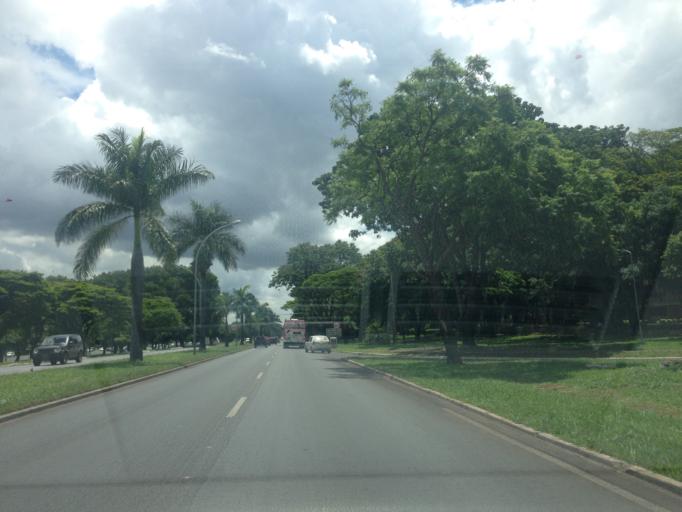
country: BR
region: Federal District
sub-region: Brasilia
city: Brasilia
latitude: -15.8285
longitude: -47.9180
